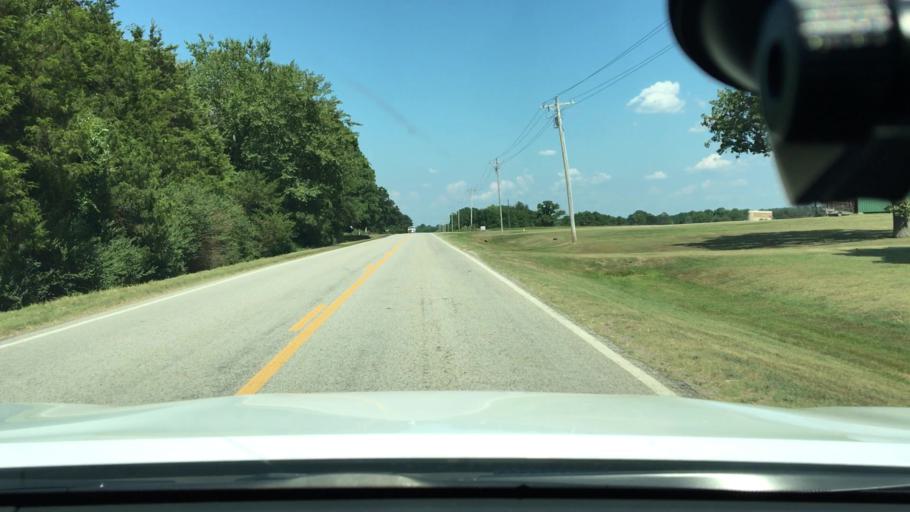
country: US
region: Arkansas
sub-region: Johnson County
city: Coal Hill
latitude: 35.3511
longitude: -93.5815
